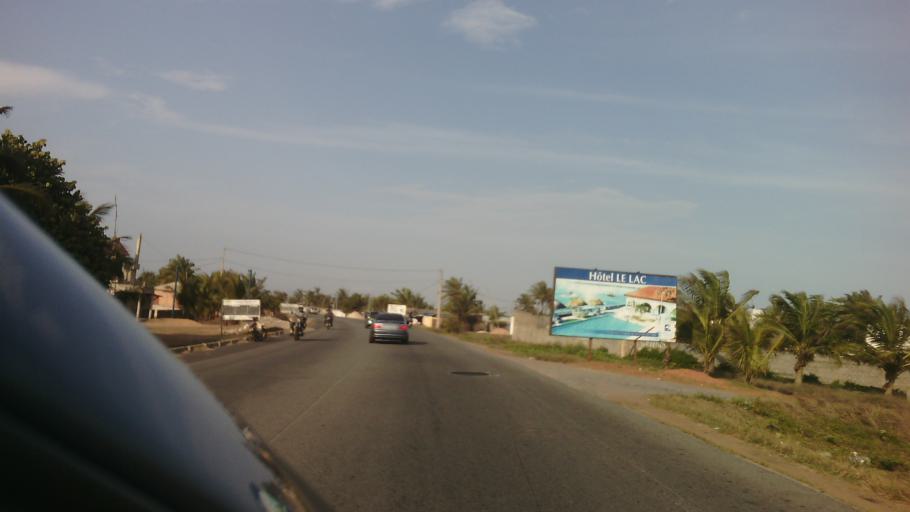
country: TG
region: Maritime
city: Lome
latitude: 6.1809
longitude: 1.3902
